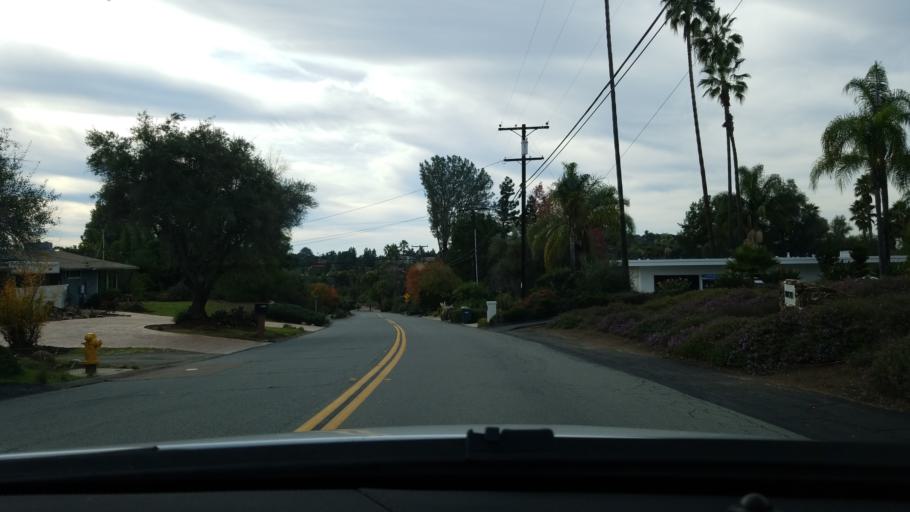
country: US
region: California
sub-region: San Diego County
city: Casa de Oro-Mount Helix
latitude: 32.7717
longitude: -116.9532
